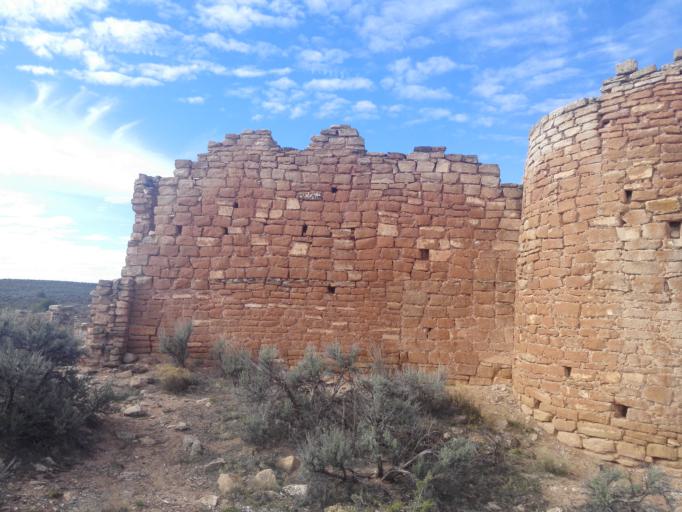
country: US
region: Colorado
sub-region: Montezuma County
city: Towaoc
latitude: 37.3860
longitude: -109.0806
